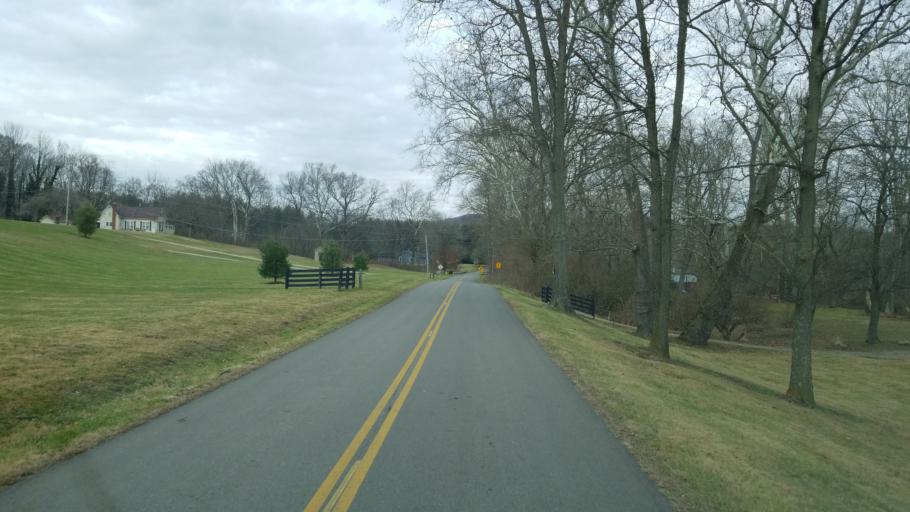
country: US
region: Ohio
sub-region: Highland County
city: Greenfield
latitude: 39.2322
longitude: -83.2900
